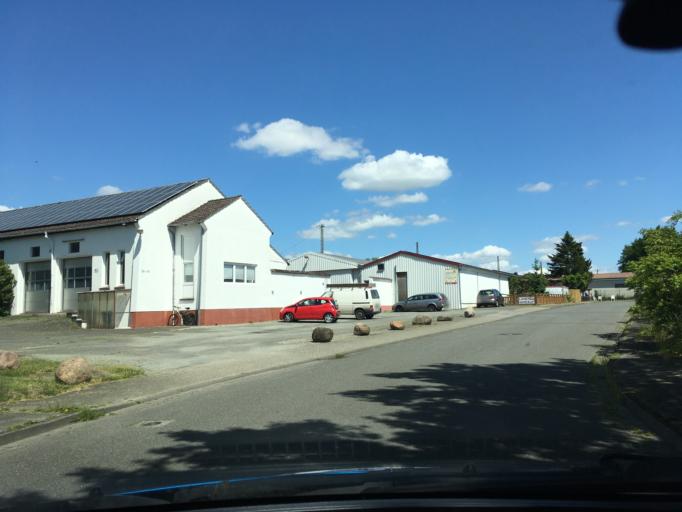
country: DE
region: Lower Saxony
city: Uelzen
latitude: 52.9601
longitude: 10.5426
